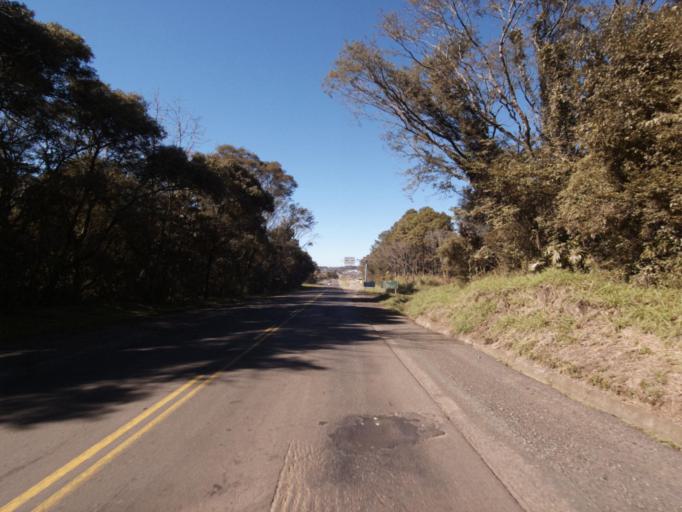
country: BR
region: Santa Catarina
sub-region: Sao Lourenco Do Oeste
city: Sao Lourenco dOeste
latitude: -26.7644
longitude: -53.2174
